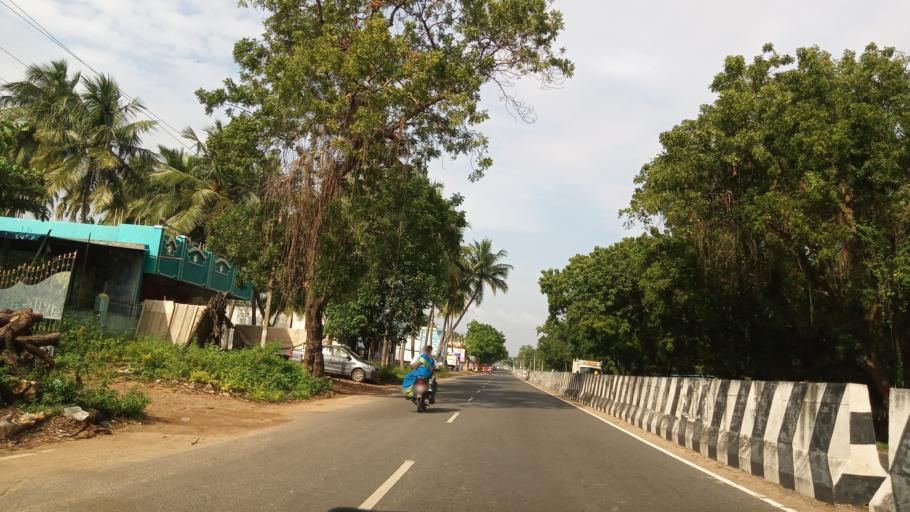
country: IN
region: Tamil Nadu
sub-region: Villupuram
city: Auroville
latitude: 12.0461
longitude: 79.8704
